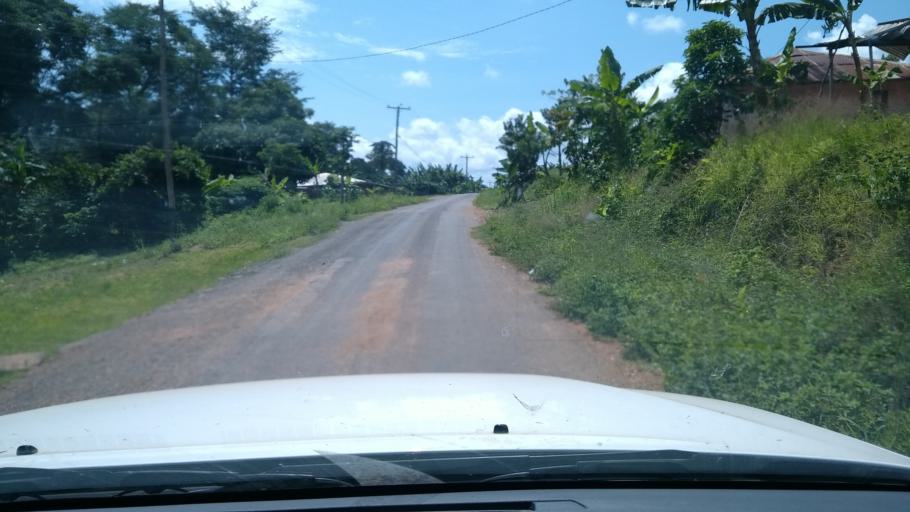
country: CM
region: Centre
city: Evodoula
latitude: 4.1456
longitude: 11.2766
